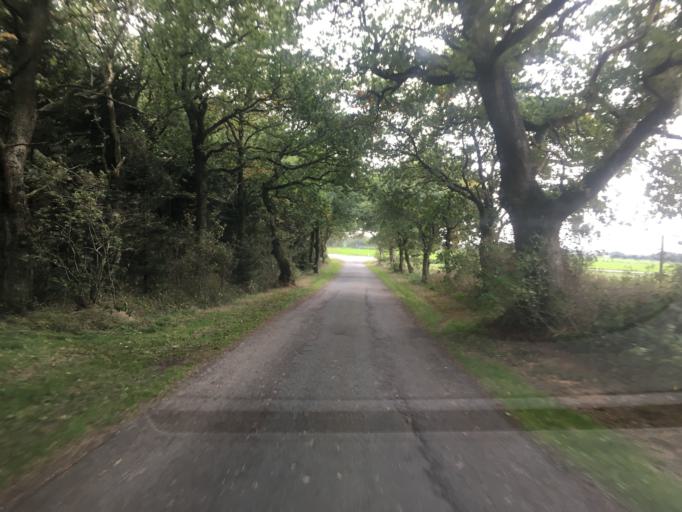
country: DK
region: South Denmark
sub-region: Tonder Kommune
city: Logumkloster
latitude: 55.0488
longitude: 9.0694
